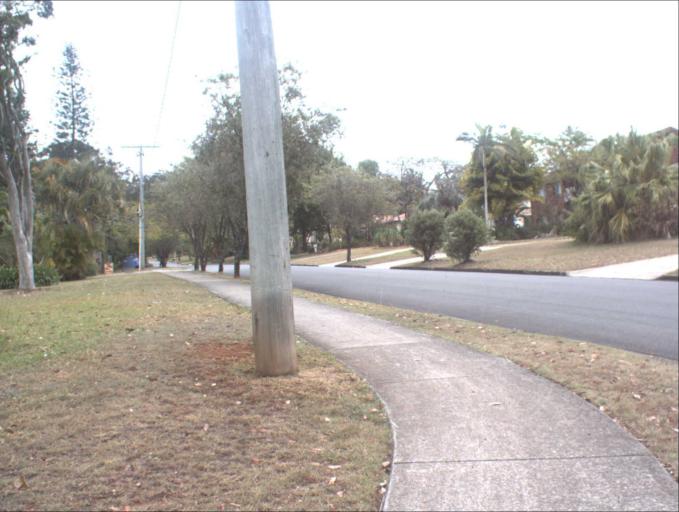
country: AU
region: Queensland
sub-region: Logan
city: Slacks Creek
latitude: -27.6701
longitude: 153.1758
